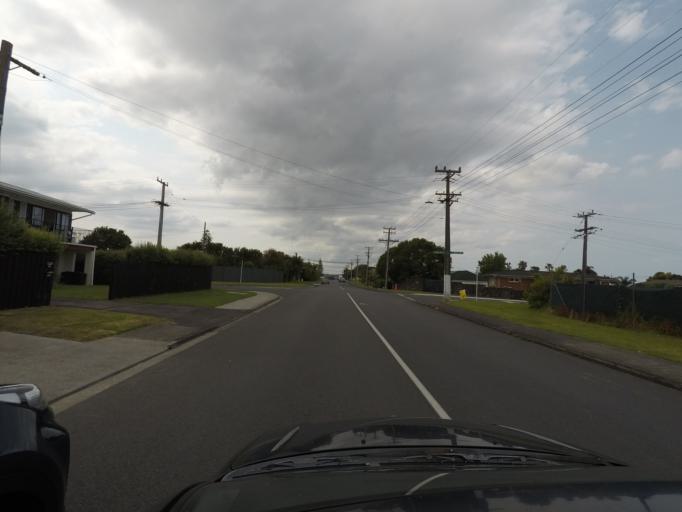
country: NZ
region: Auckland
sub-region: Auckland
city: Rosebank
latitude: -36.8291
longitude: 174.6466
